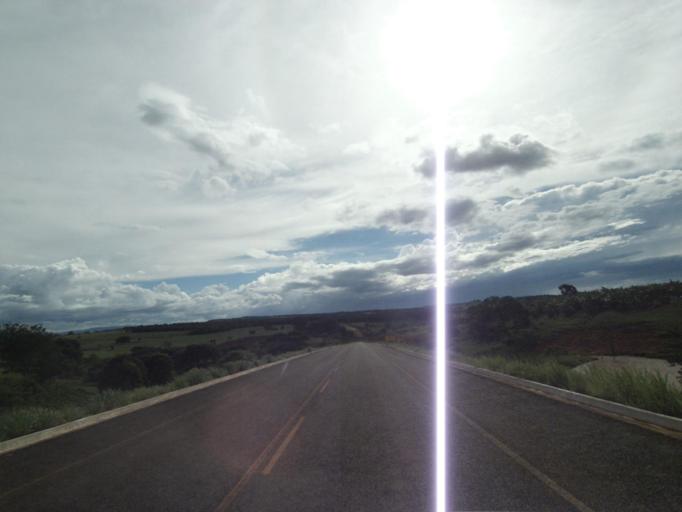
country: BR
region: Goias
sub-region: Jaragua
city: Jaragua
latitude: -15.8691
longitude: -49.4096
